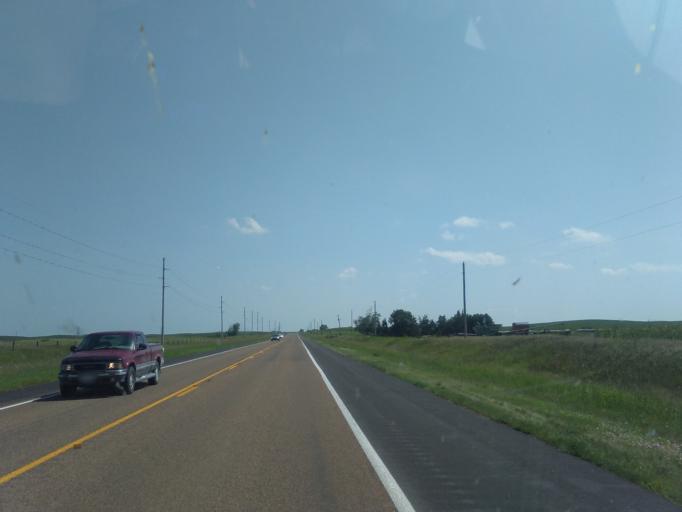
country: US
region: Nebraska
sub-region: Phelps County
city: Holdrege
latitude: 40.6529
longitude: -99.3806
